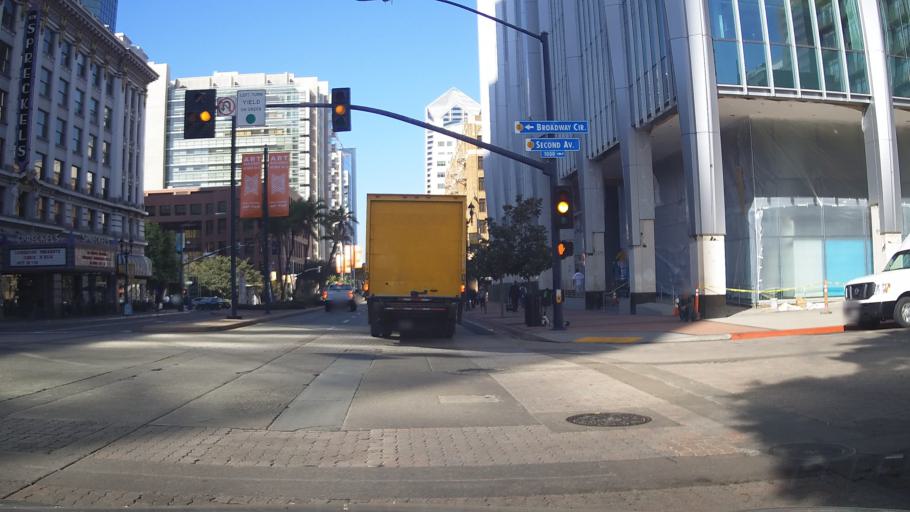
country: US
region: California
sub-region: San Diego County
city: San Diego
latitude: 32.7158
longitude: -117.1627
